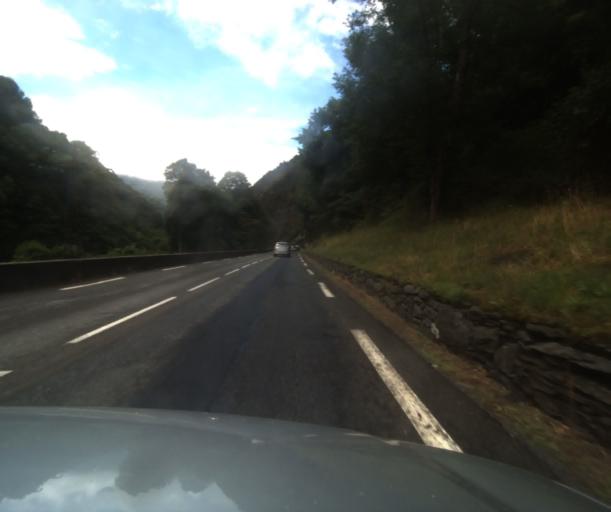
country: FR
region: Midi-Pyrenees
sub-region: Departement des Hautes-Pyrenees
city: Pierrefitte-Nestalas
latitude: 42.9455
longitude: -0.0554
